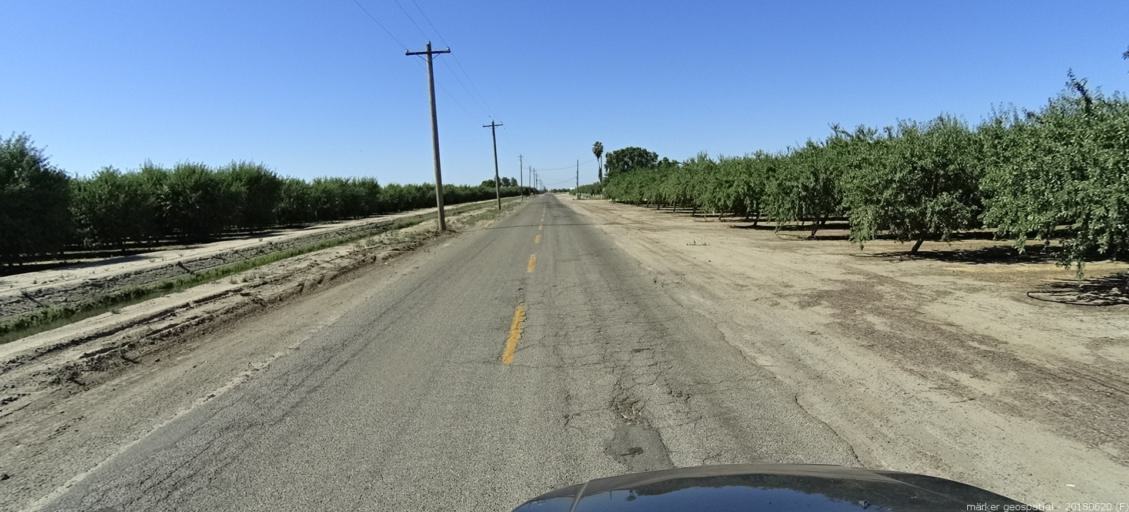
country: US
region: California
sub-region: Madera County
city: Parkwood
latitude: 36.8947
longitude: -120.0376
